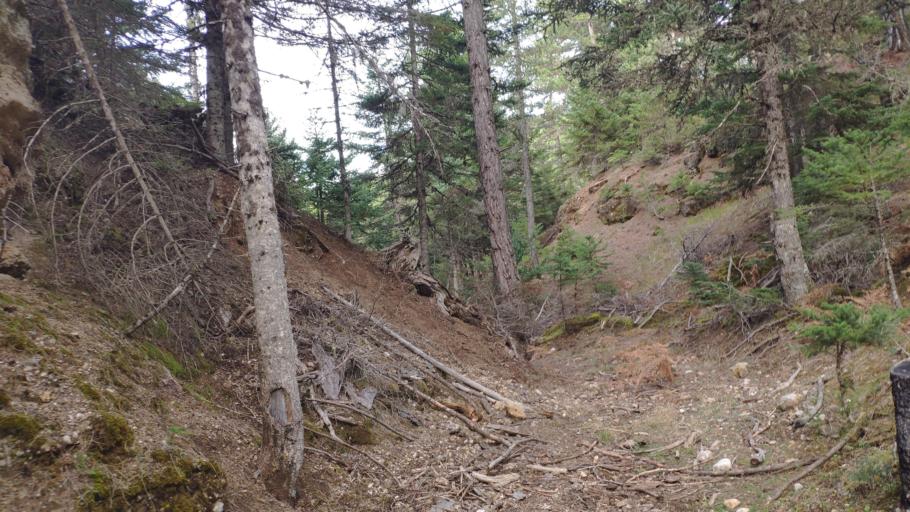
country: GR
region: West Greece
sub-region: Nomos Achaias
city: Aiyira
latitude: 38.0304
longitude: 22.3735
